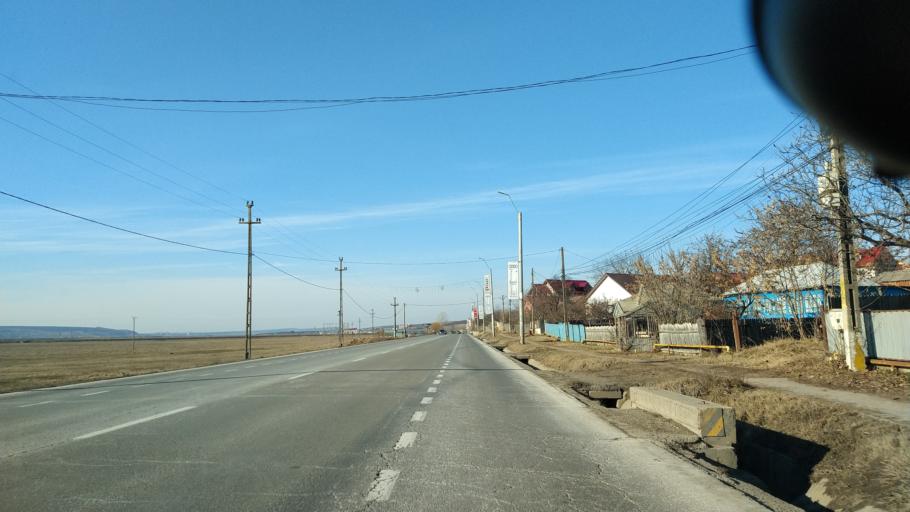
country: RO
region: Iasi
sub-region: Comuna Letcani
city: Letcani
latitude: 47.1999
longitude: 27.3894
